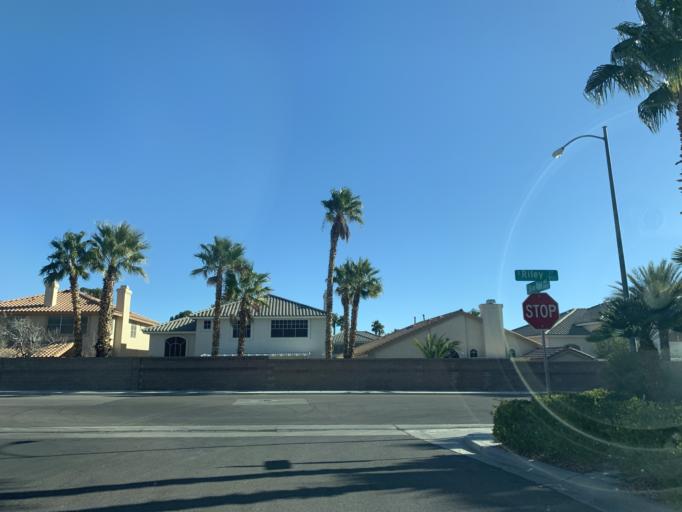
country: US
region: Nevada
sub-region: Clark County
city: Spring Valley
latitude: 36.1197
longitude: -115.2838
